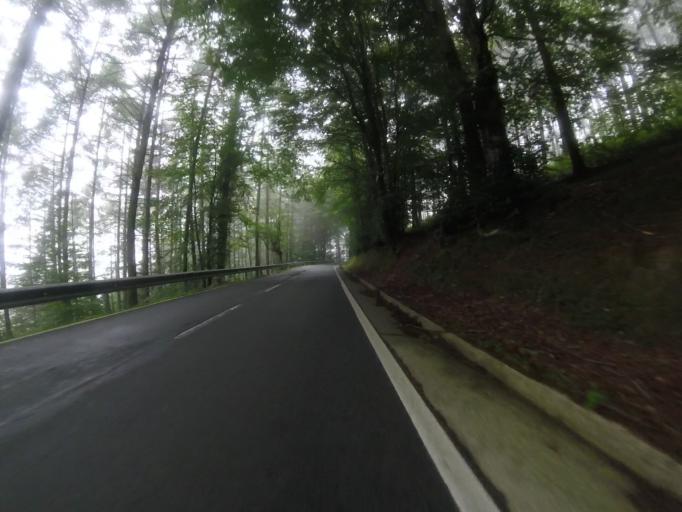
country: ES
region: Navarre
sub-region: Provincia de Navarra
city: Leitza
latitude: 43.0856
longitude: -1.8709
